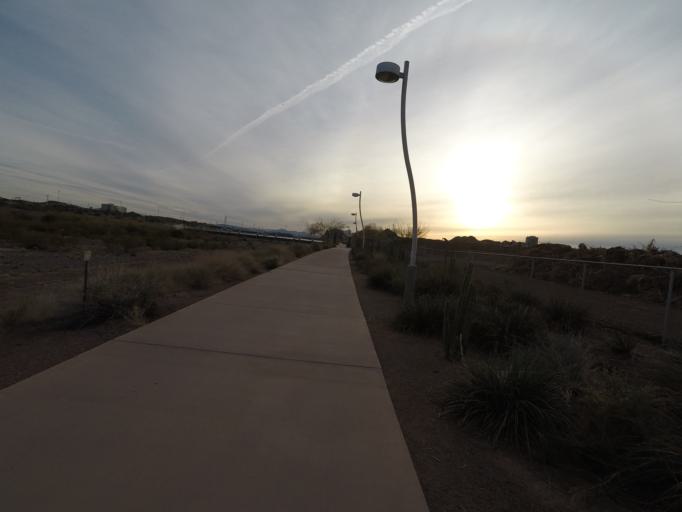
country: US
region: Arizona
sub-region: Maricopa County
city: Tempe Junction
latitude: 33.4333
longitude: -111.9562
